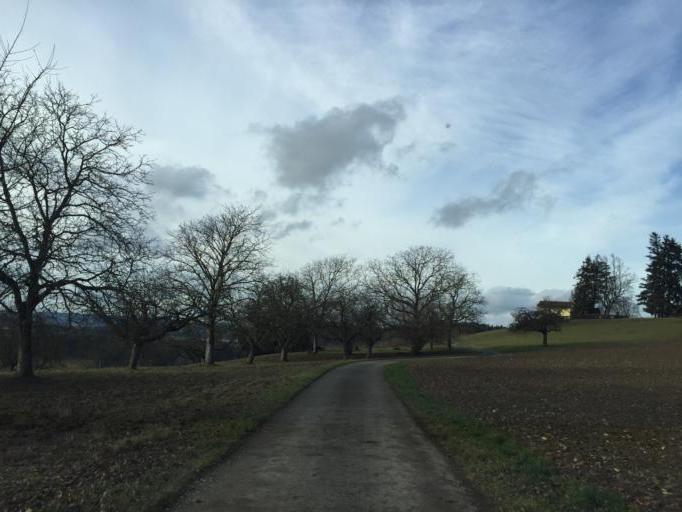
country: CH
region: Zurich
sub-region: Bezirk Andelfingen
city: Kleinandelfingen
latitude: 47.6327
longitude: 8.6955
